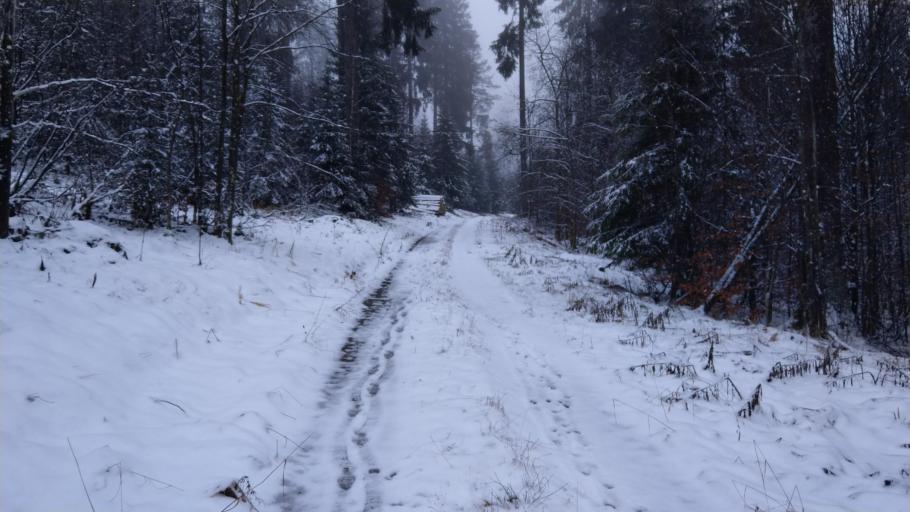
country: DE
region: North Rhine-Westphalia
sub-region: Regierungsbezirk Arnsberg
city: Erndtebruck
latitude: 50.9793
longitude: 8.1909
